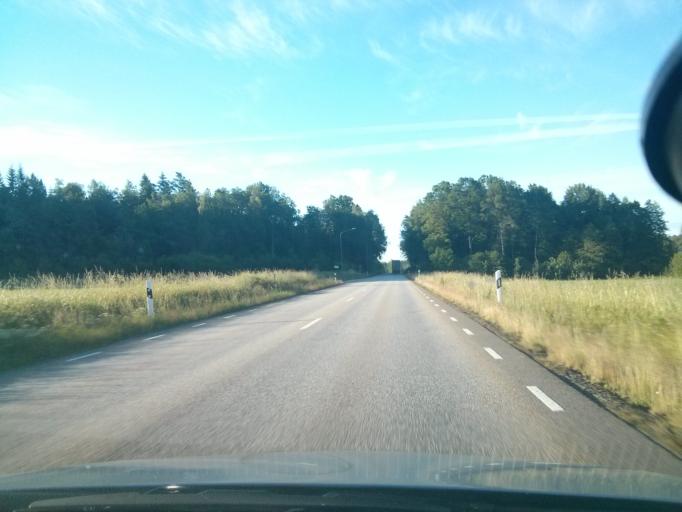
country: SE
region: Blekinge
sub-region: Ronneby Kommun
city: Brakne-Hoby
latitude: 56.3044
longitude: 15.1900
